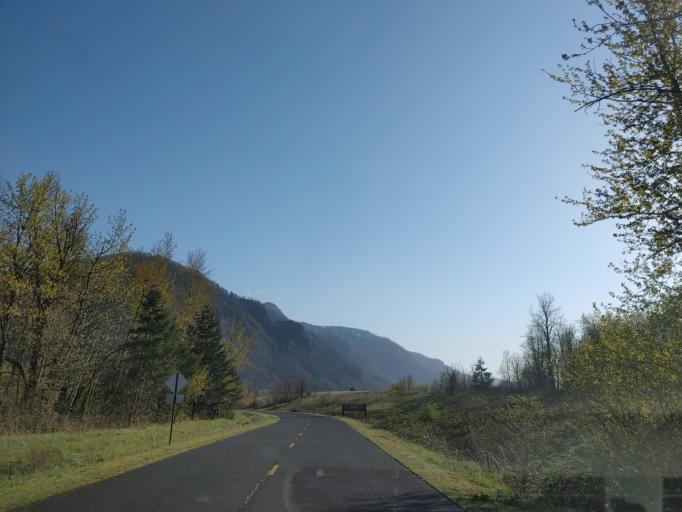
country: US
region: Oregon
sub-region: Hood River County
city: Cascade Locks
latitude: 45.6365
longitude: -121.9681
